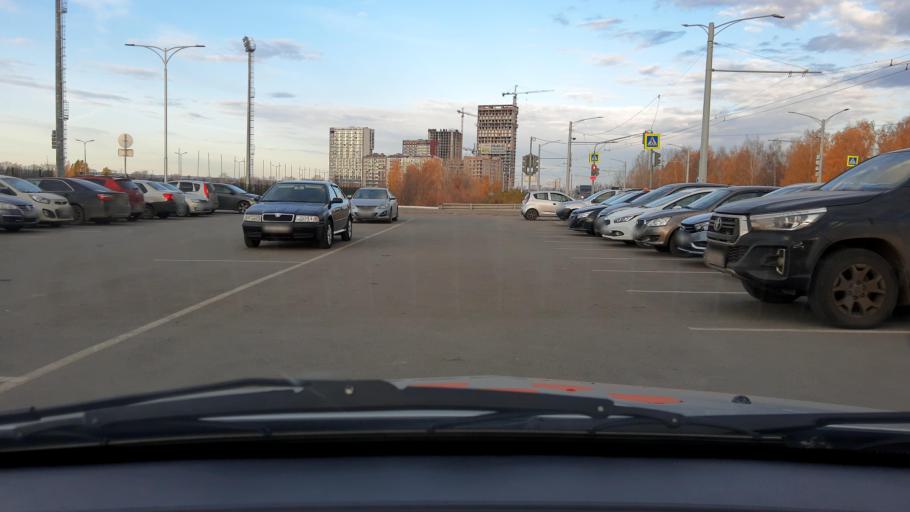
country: RU
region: Bashkortostan
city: Mikhaylovka
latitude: 54.7695
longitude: 55.9124
